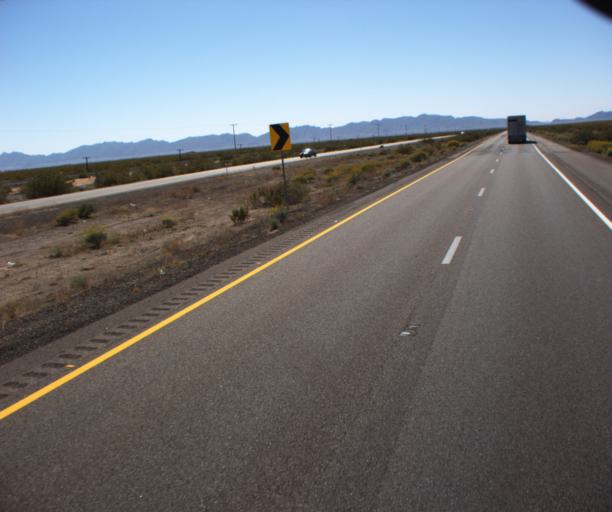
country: US
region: Arizona
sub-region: Yuma County
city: Wellton
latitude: 32.7893
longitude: -113.5608
